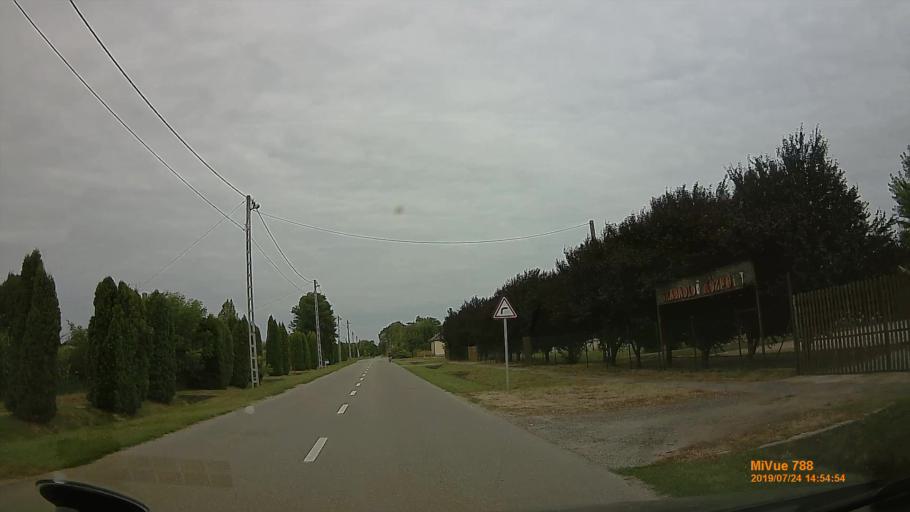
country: HU
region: Szabolcs-Szatmar-Bereg
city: Aranyosapati
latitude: 48.2586
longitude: 22.3122
